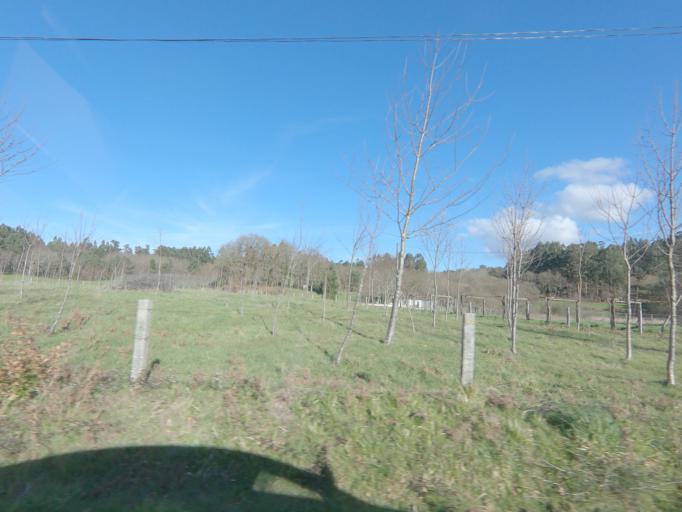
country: ES
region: Galicia
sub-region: Provincia da Coruna
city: Ribeira
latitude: 42.7134
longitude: -8.4345
